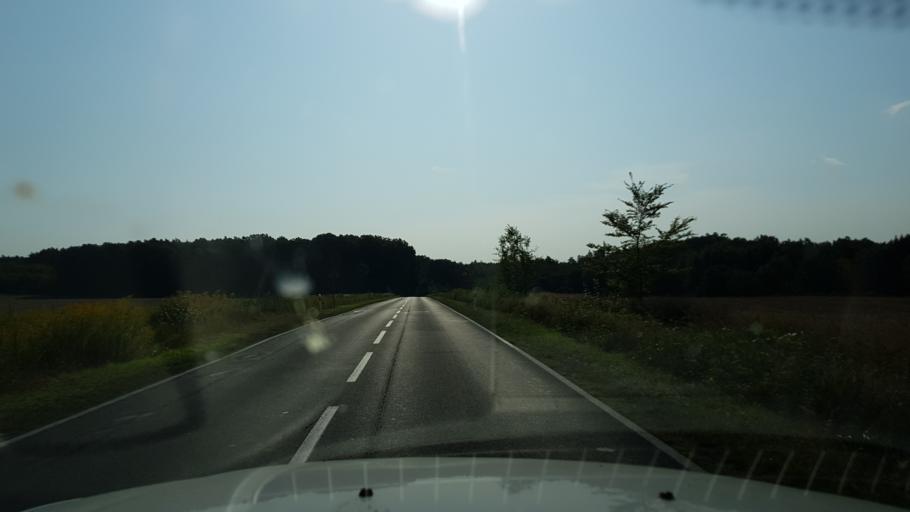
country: PL
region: West Pomeranian Voivodeship
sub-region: Powiat lobeski
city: Resko
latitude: 53.7735
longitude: 15.4398
